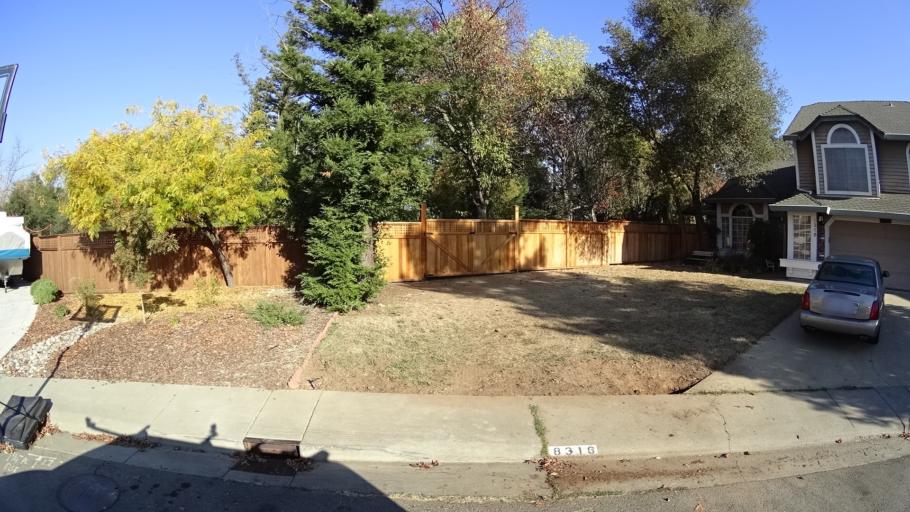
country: US
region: California
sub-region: Sacramento County
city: Citrus Heights
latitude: 38.7174
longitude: -121.2643
